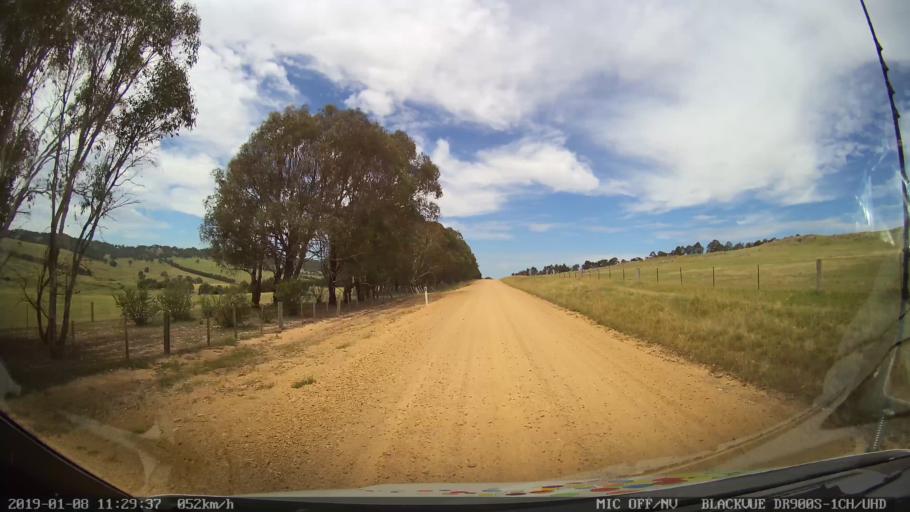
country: AU
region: New South Wales
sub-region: Guyra
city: Guyra
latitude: -30.3016
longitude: 151.5480
